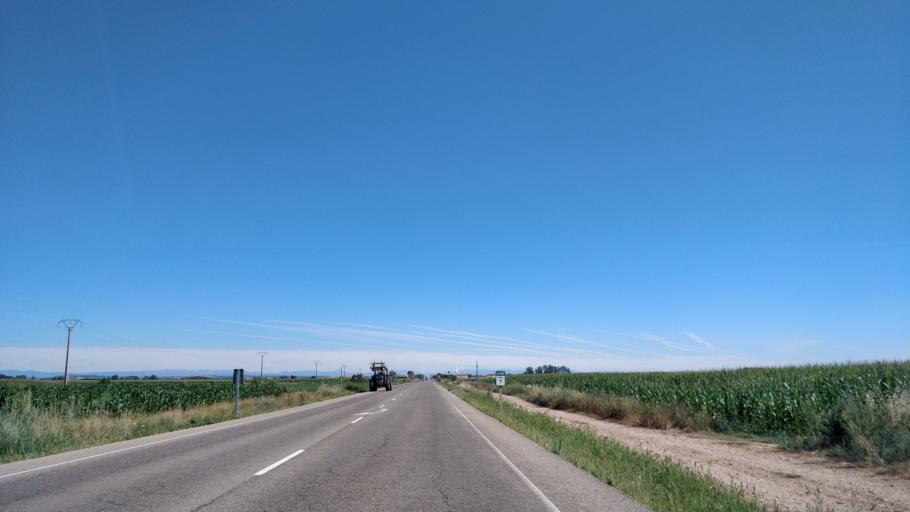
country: ES
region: Castille and Leon
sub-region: Provincia de Leon
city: San Cristobal de la Polantera
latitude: 42.3660
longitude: -5.8896
